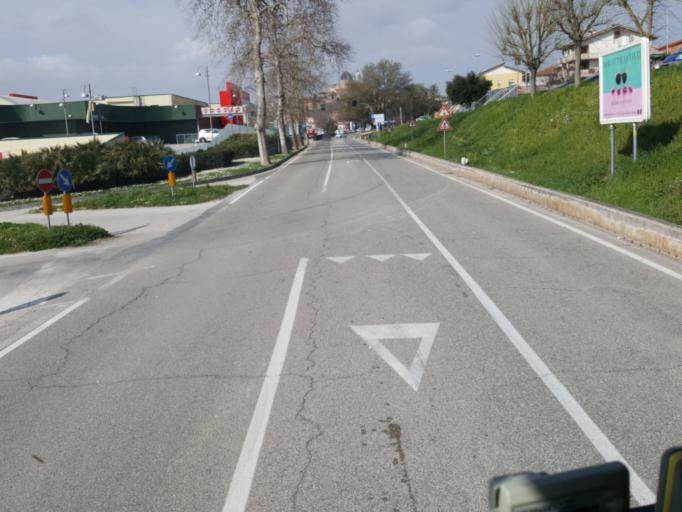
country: IT
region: The Marches
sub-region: Provincia di Ancona
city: Loreto Stazione
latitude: 43.4406
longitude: 13.6290
